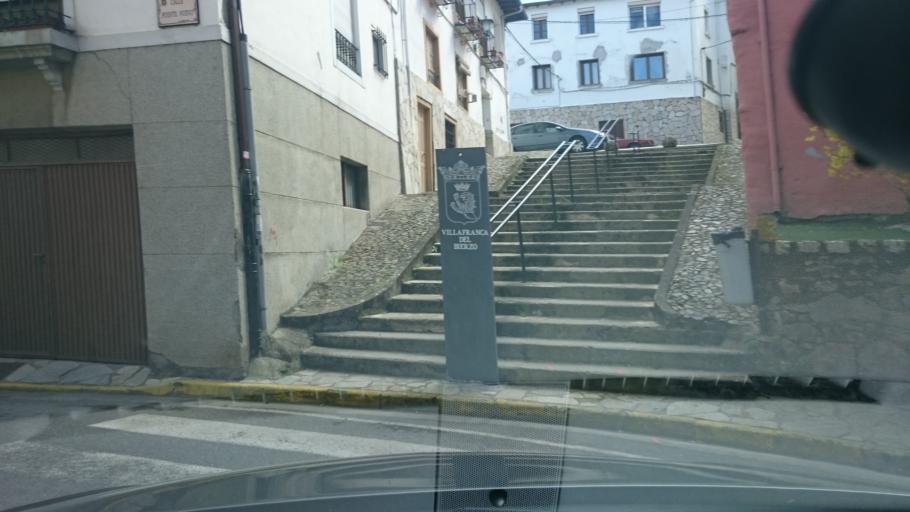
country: ES
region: Castille and Leon
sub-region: Provincia de Leon
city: Villafranca del Bierzo
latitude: 42.6055
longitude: -6.8105
